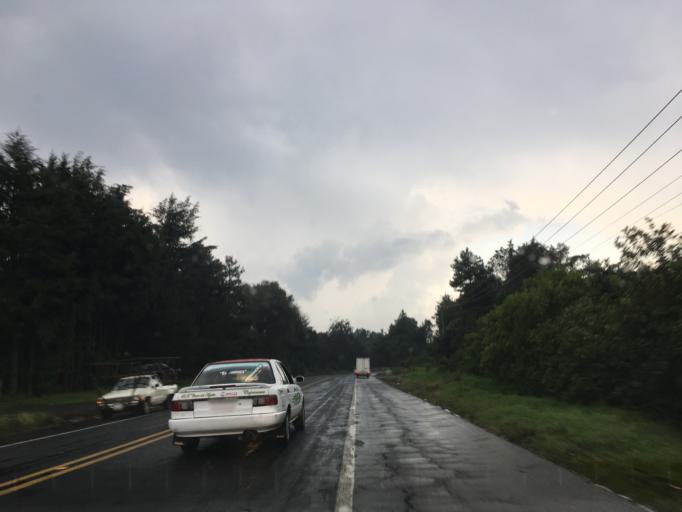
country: MX
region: Michoacan
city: Capacuaro
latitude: 19.5275
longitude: -102.0770
